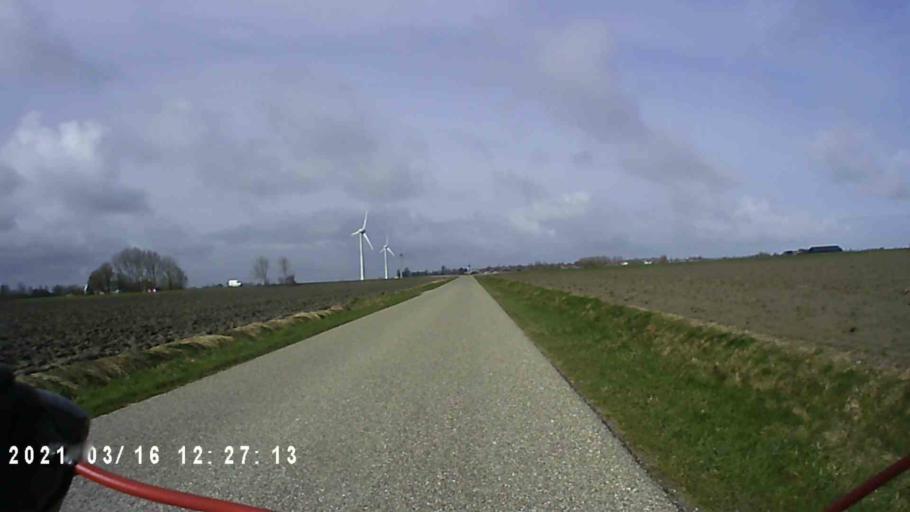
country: NL
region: Friesland
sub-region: Gemeente Leeuwarderadeel
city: Stiens
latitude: 53.2965
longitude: 5.7406
